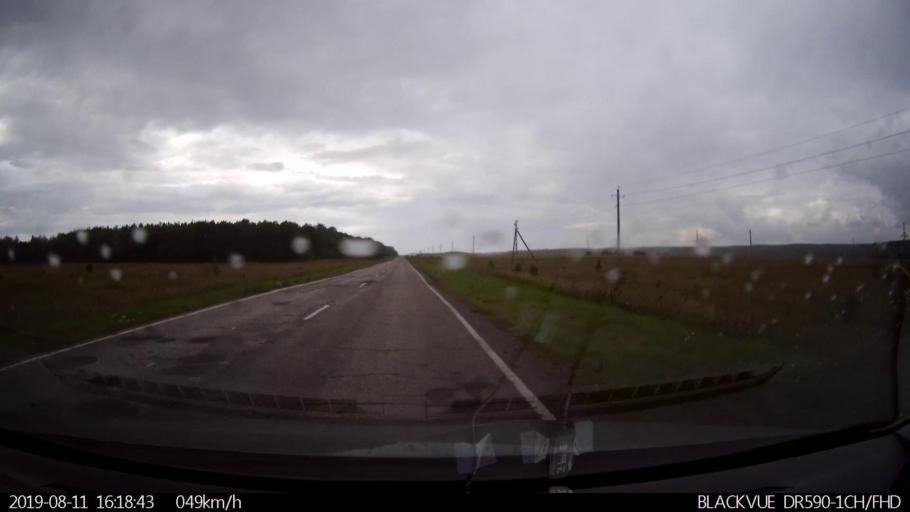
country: RU
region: Ulyanovsk
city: Mayna
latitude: 54.0572
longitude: 47.6108
